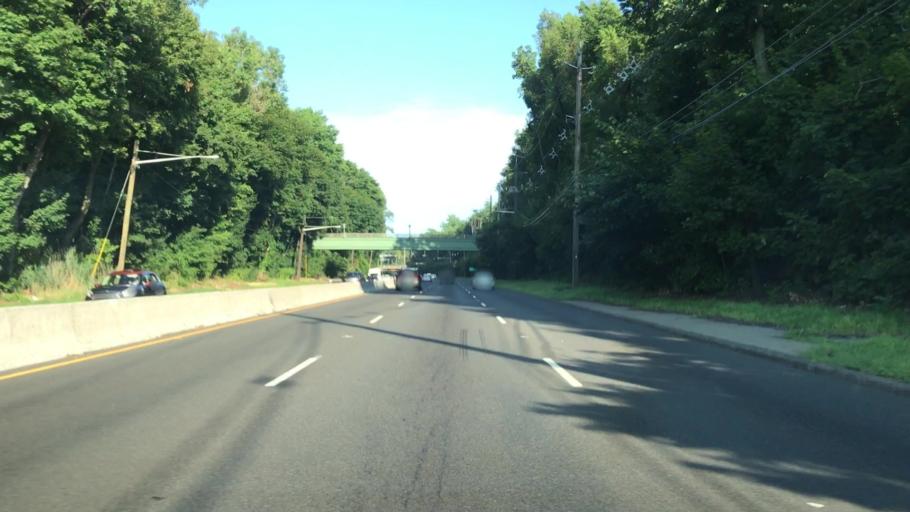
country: US
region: New Jersey
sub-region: Bergen County
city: Teaneck
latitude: 40.8978
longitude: -74.0236
